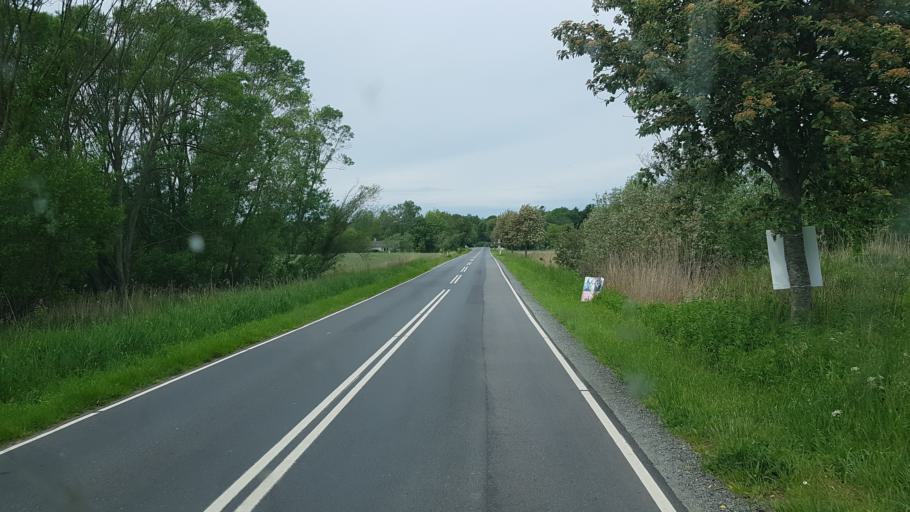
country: DK
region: South Denmark
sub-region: Nordfyns Kommune
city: Sonderso
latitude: 55.5716
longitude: 10.2024
